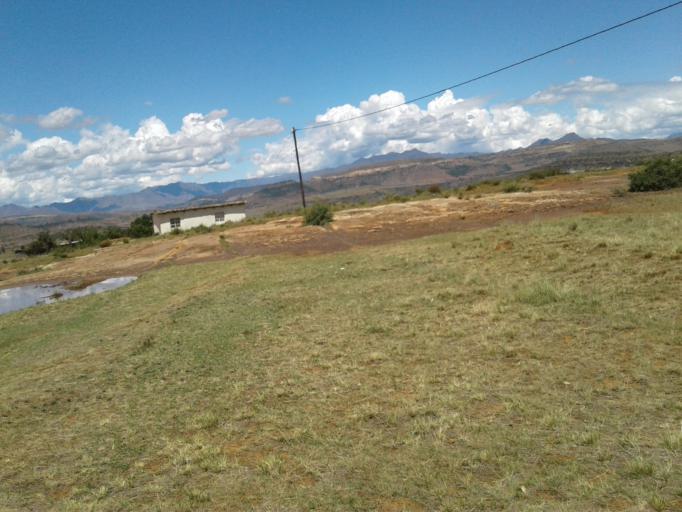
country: LS
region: Quthing
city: Quthing
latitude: -30.3776
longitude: 27.5569
